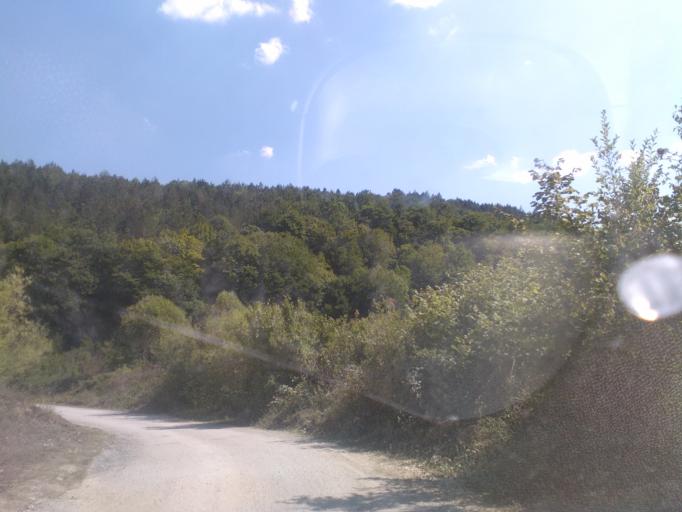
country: BA
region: Federation of Bosnia and Herzegovina
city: Orasac
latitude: 44.6209
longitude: 16.0618
